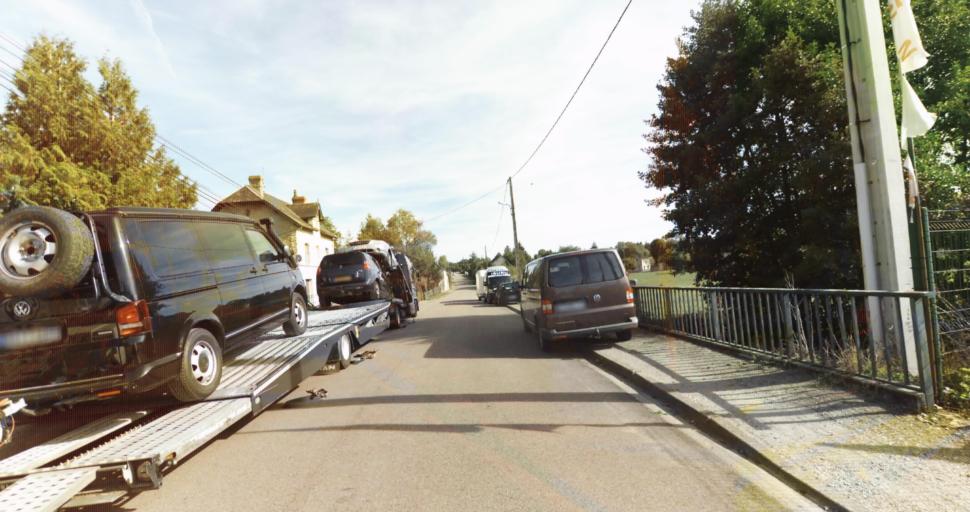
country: FR
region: Lower Normandy
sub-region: Departement de l'Orne
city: Gace
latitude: 48.7066
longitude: 0.2239
